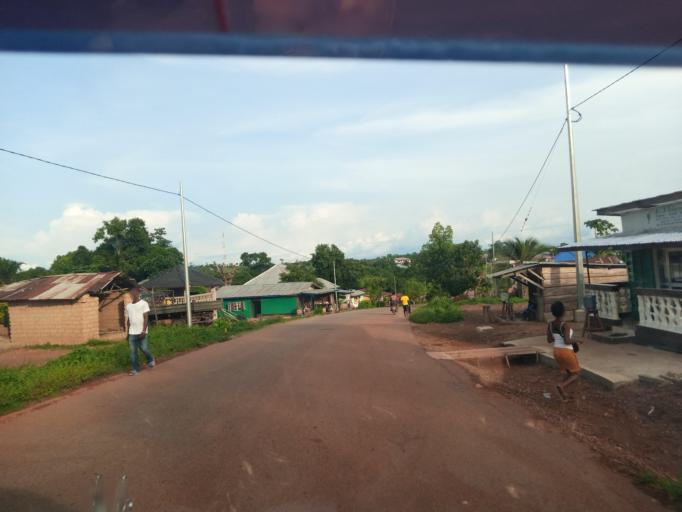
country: SL
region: Southern Province
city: Largo
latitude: 8.2004
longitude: -12.0598
